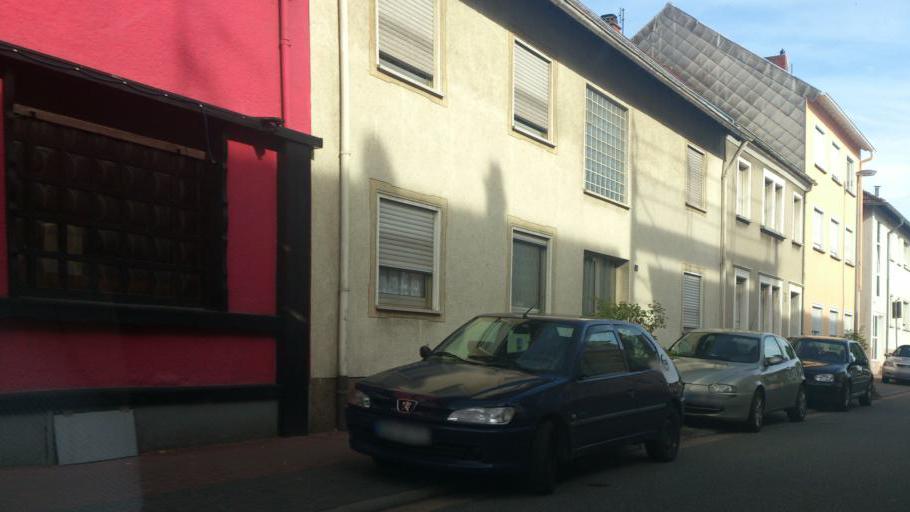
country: DE
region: Saarland
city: Homburg
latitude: 49.3351
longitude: 7.3355
